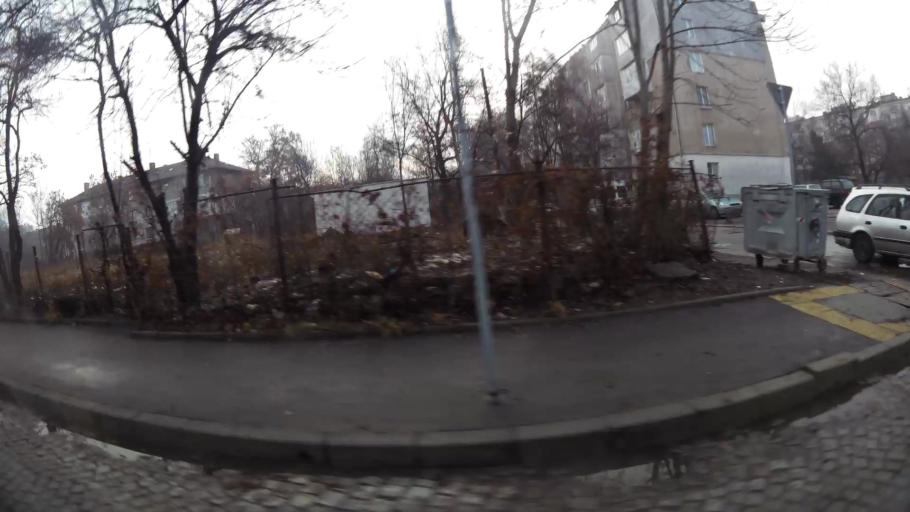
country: BG
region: Sofia-Capital
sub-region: Stolichna Obshtina
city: Sofia
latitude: 42.7302
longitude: 23.3095
